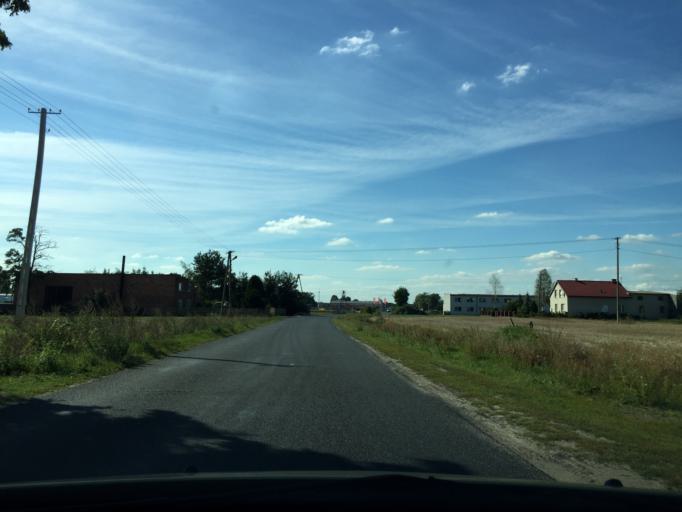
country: PL
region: Greater Poland Voivodeship
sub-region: Powiat kaliski
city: Stawiszyn
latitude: 51.9189
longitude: 18.1226
